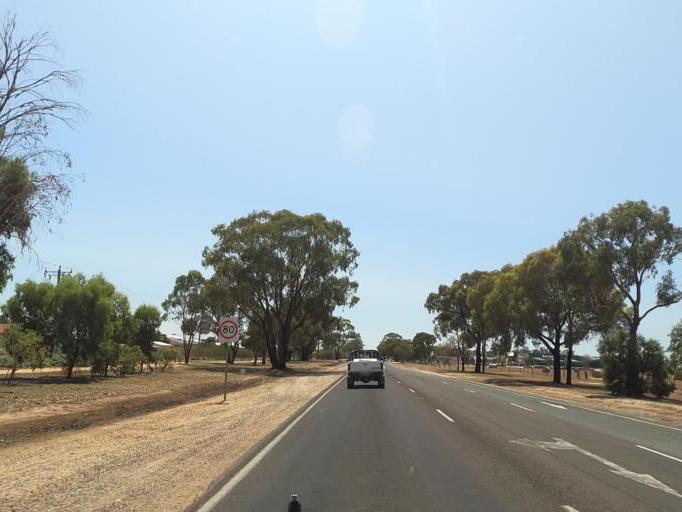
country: AU
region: Victoria
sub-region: Moira
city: Yarrawonga
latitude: -36.0126
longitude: 146.0213
